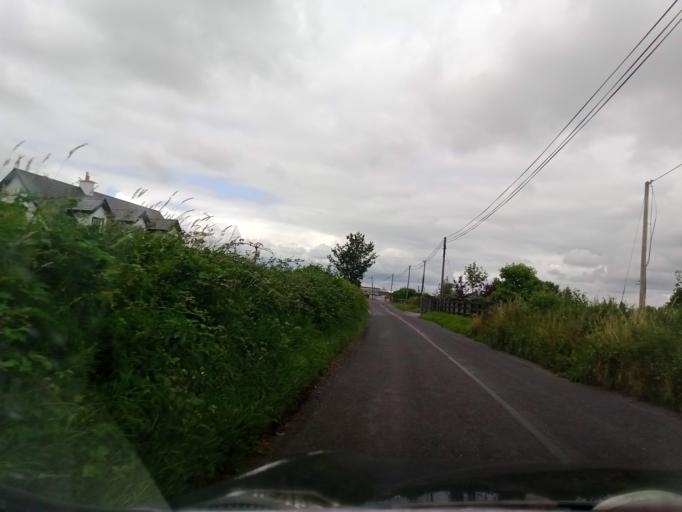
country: IE
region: Leinster
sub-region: Laois
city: Stradbally
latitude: 52.9730
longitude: -7.1797
